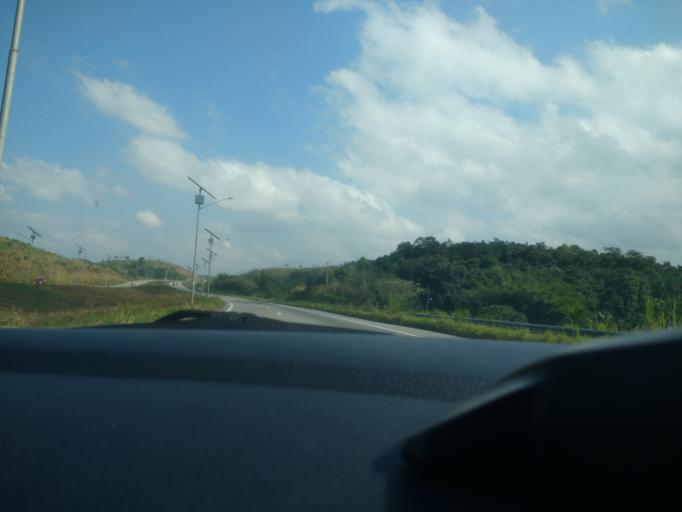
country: BR
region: Rio de Janeiro
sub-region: Queimados
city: Queimados
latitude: -22.6866
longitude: -43.5054
